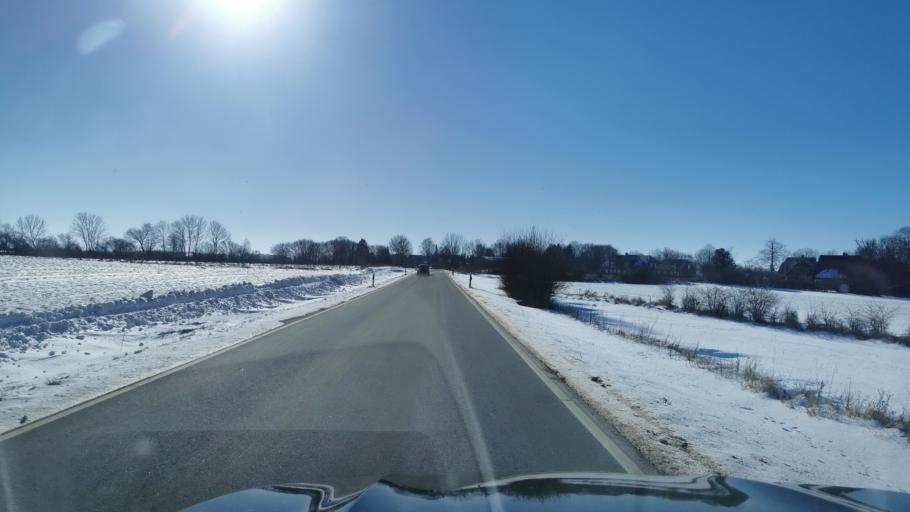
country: DE
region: Schleswig-Holstein
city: Langballig
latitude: 54.8147
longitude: 9.6405
